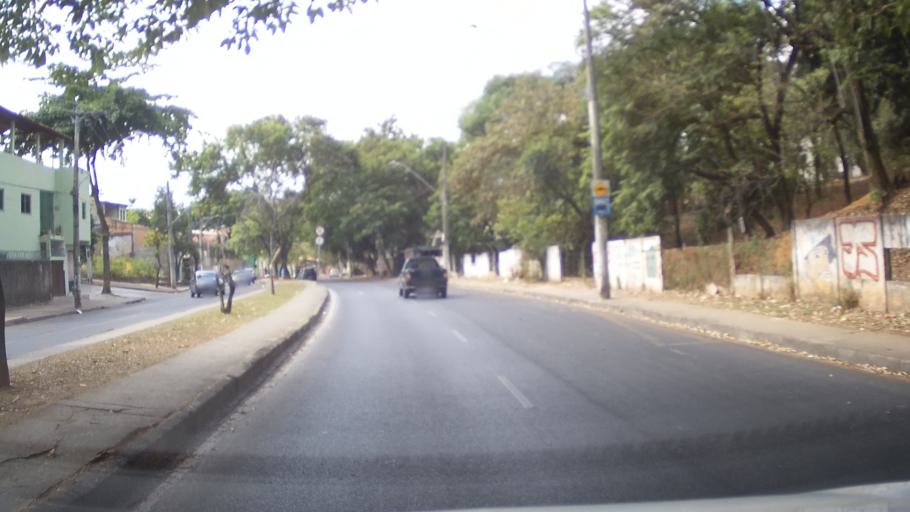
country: BR
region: Minas Gerais
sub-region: Belo Horizonte
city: Belo Horizonte
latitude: -19.8331
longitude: -43.9710
